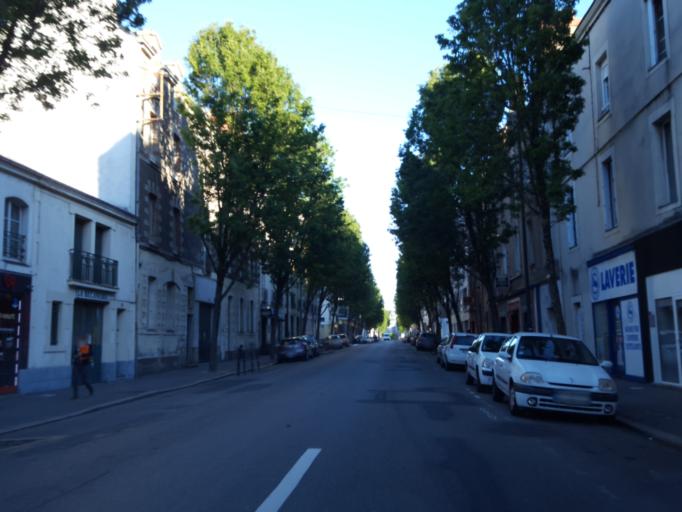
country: FR
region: Pays de la Loire
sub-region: Departement de la Loire-Atlantique
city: Nantes
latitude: 47.2100
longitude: -1.5706
